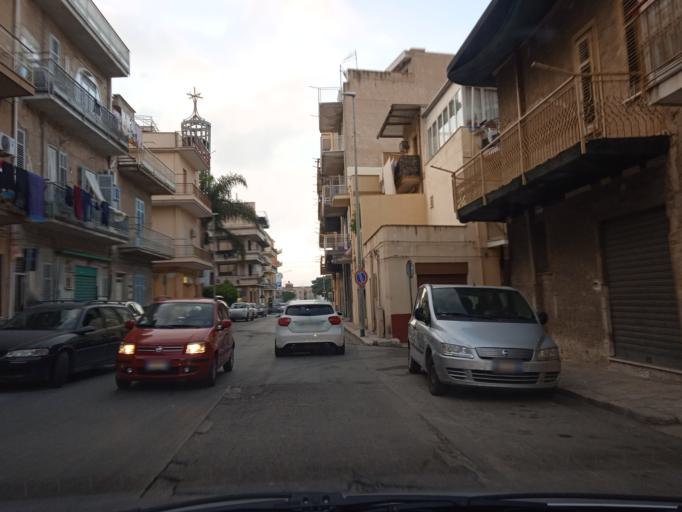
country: IT
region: Sicily
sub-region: Palermo
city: Villabate
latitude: 38.0797
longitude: 13.4367
